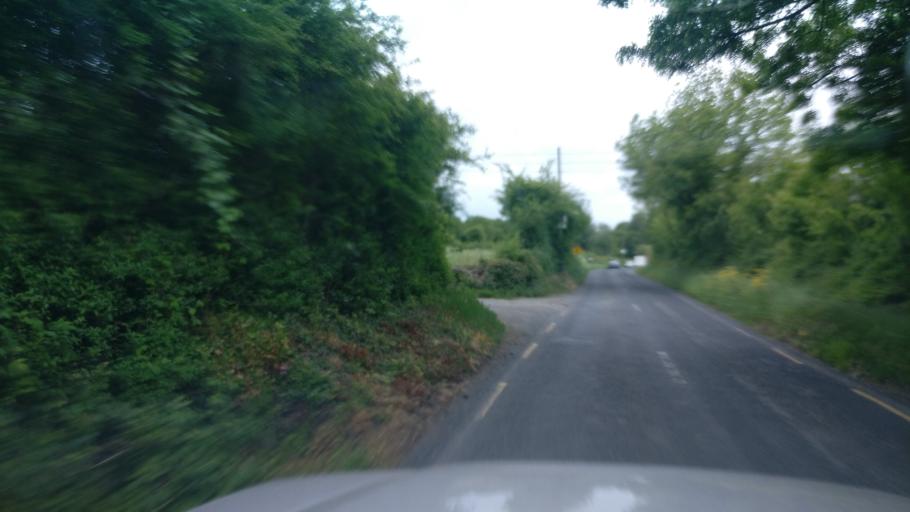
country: IE
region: Connaught
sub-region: County Galway
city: Portumna
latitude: 53.1176
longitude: -8.3093
